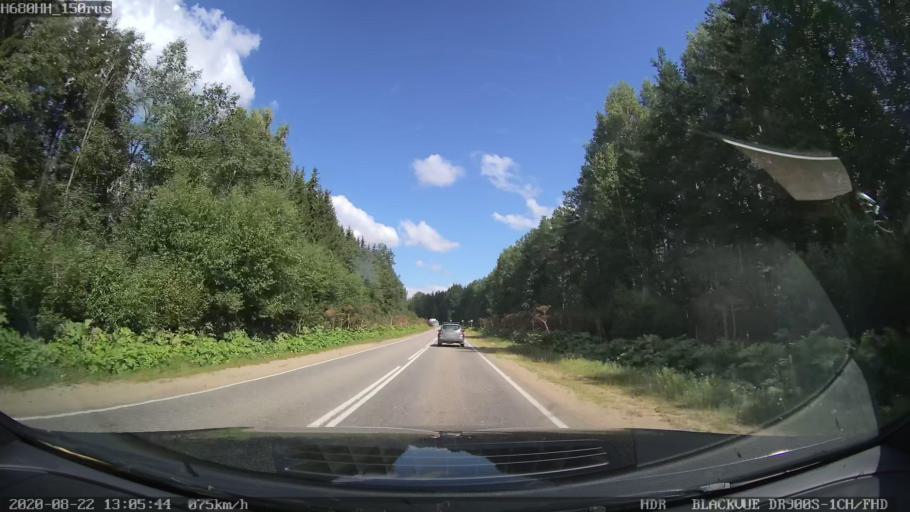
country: RU
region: Tverskaya
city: Bezhetsk
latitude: 57.6747
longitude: 36.4516
